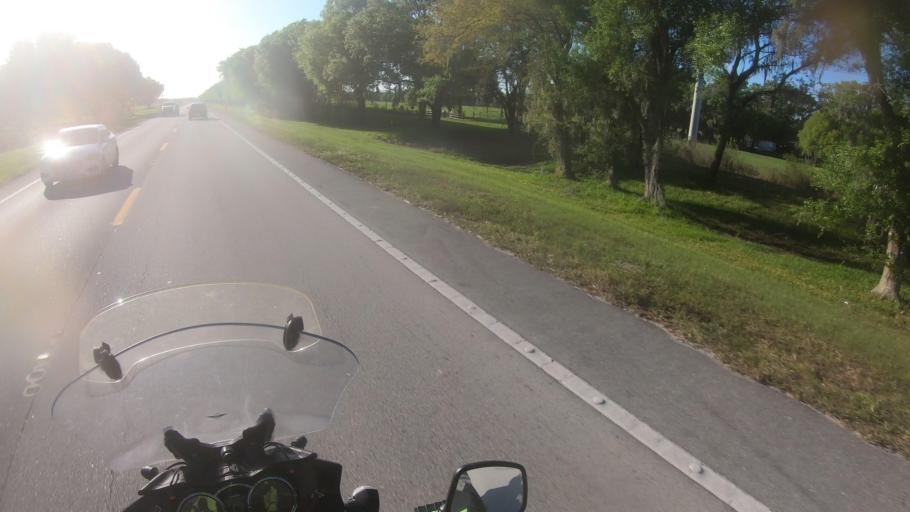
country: US
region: Florida
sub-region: DeSoto County
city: Southeast Arcadia
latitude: 27.2091
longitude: -81.7748
